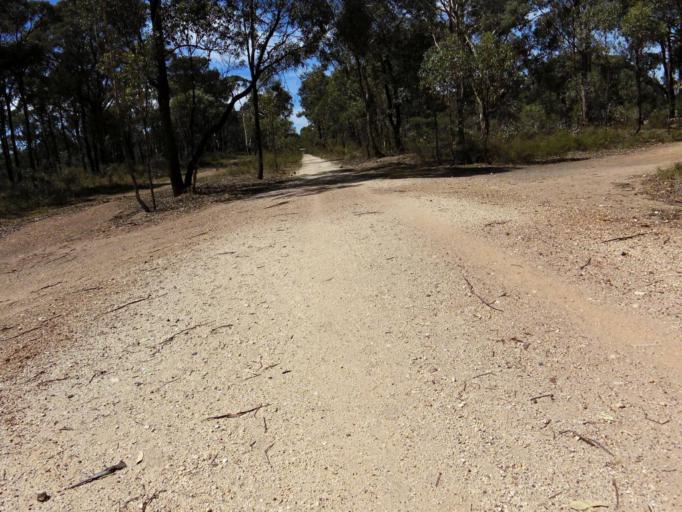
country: AU
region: Victoria
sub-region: Greater Bendigo
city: Kennington
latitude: -36.7601
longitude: 144.3353
